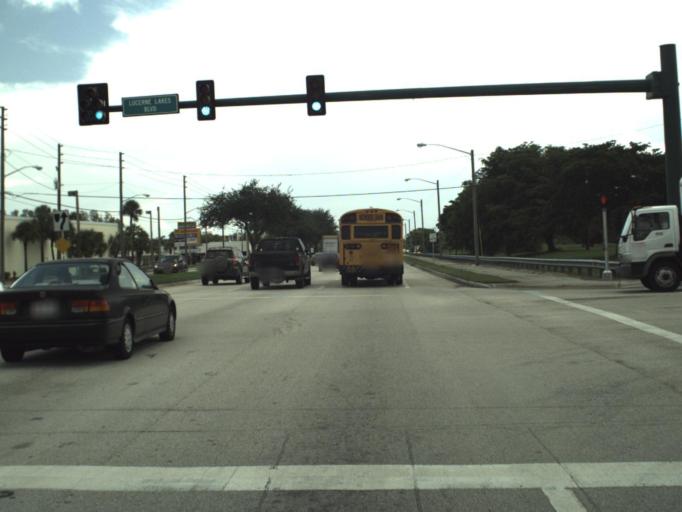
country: US
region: Florida
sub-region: Palm Beach County
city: Greenacres City
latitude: 26.6175
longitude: -80.1617
